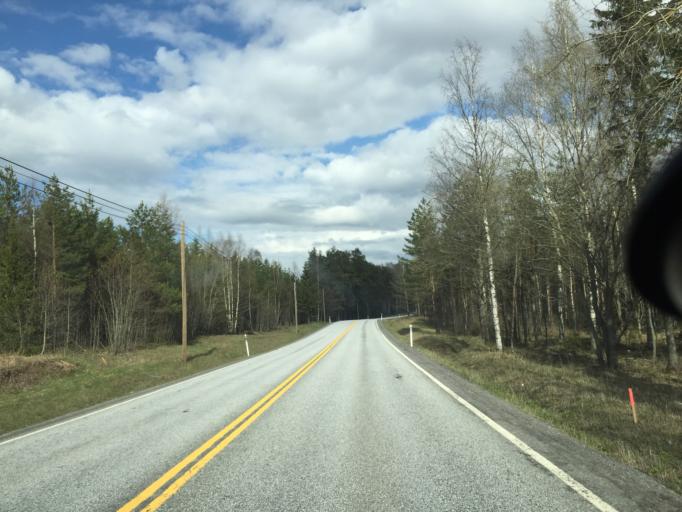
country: FI
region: Uusimaa
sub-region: Raaseporin
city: Inga
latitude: 60.1512
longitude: 23.9041
